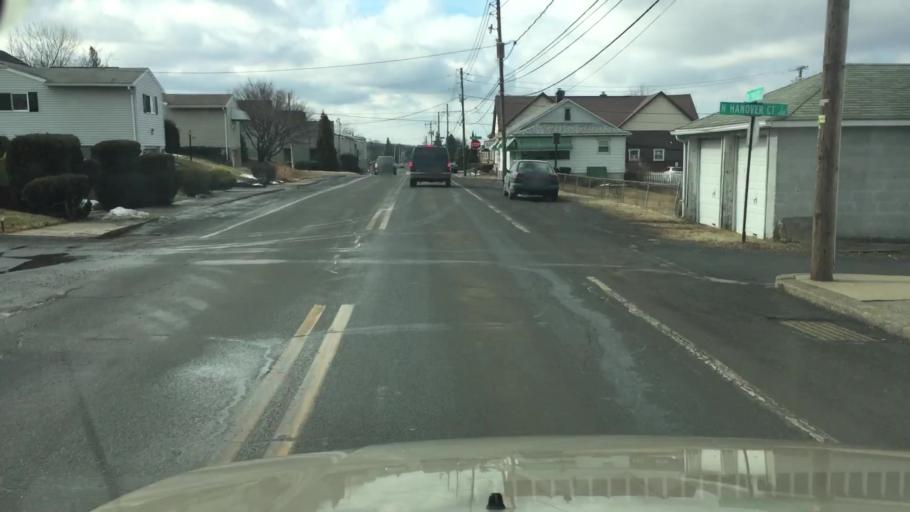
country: US
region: Pennsylvania
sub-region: Luzerne County
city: Harleigh
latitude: 40.9734
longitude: -75.9858
